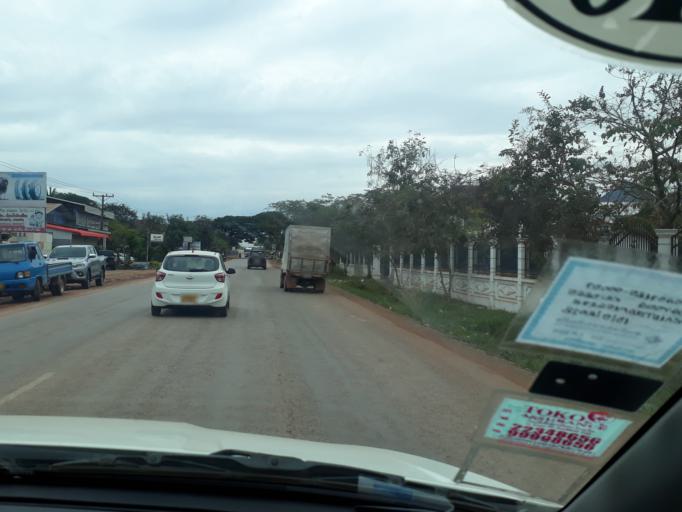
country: LA
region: Vientiane
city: Muang Phon-Hong
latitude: 18.3381
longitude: 102.4352
